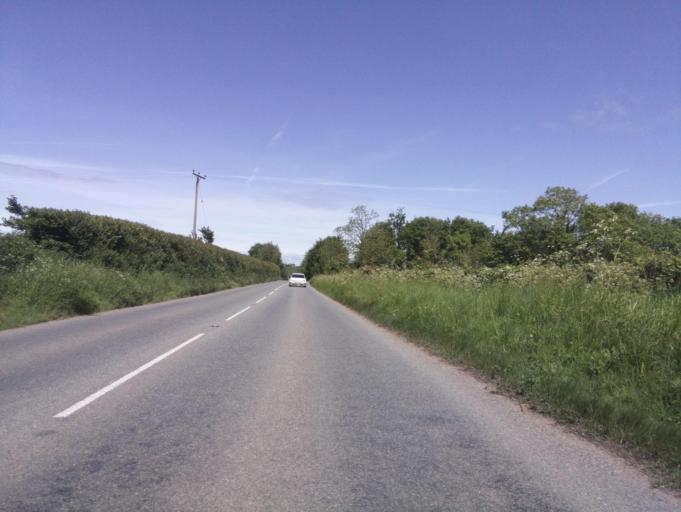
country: GB
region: England
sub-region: Devon
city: Budleigh Salterton
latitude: 50.6548
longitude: -3.3162
